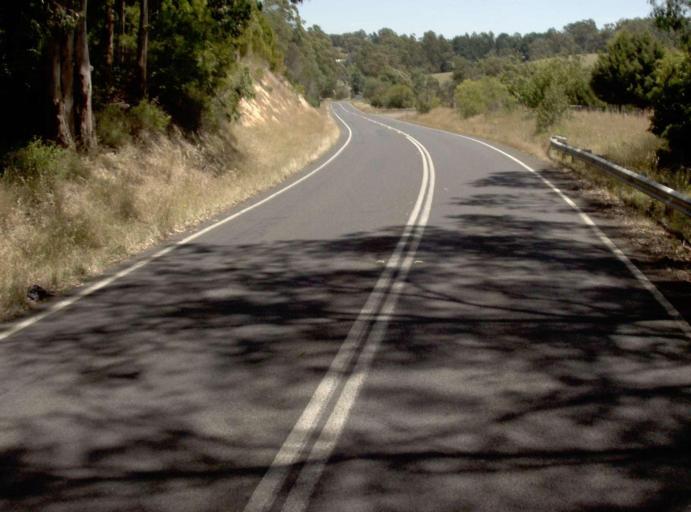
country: AU
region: Victoria
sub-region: Baw Baw
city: Warragul
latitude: -38.0639
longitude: 145.9296
